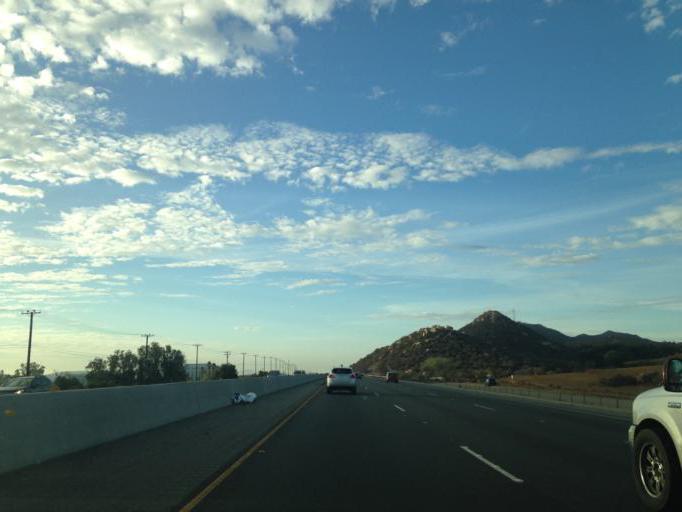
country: US
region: California
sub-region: Riverside County
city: Murrieta Hot Springs
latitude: 33.6239
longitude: -117.1711
